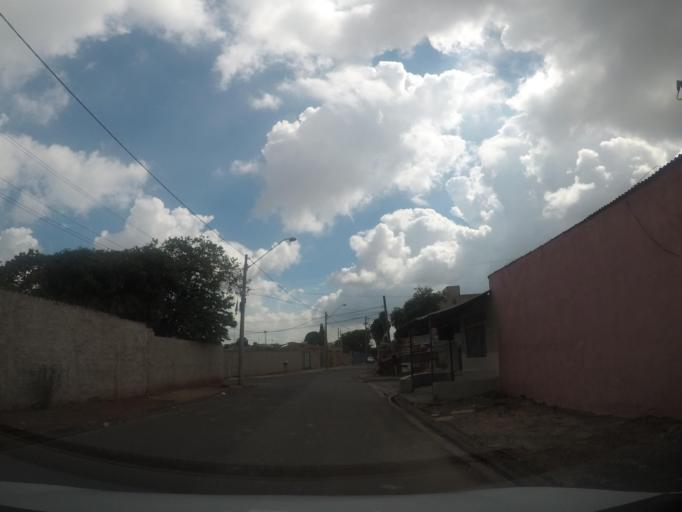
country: BR
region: Sao Paulo
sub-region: Hortolandia
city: Hortolandia
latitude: -22.8567
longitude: -47.1631
